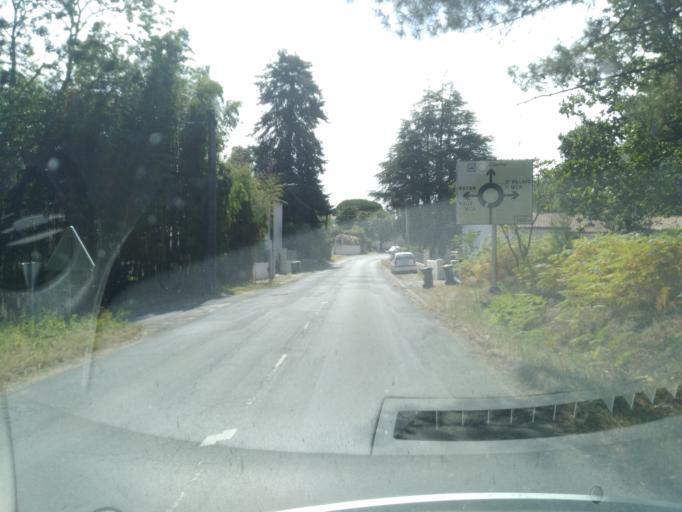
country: FR
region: Poitou-Charentes
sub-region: Departement de la Charente-Maritime
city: Vaux-sur-Mer
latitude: 45.6653
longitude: -1.0736
